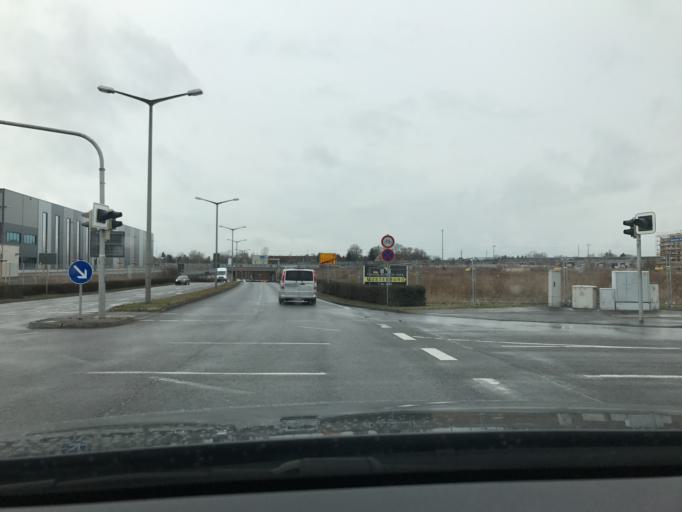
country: DE
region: Saxony
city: Rackwitz
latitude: 51.4003
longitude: 12.3932
